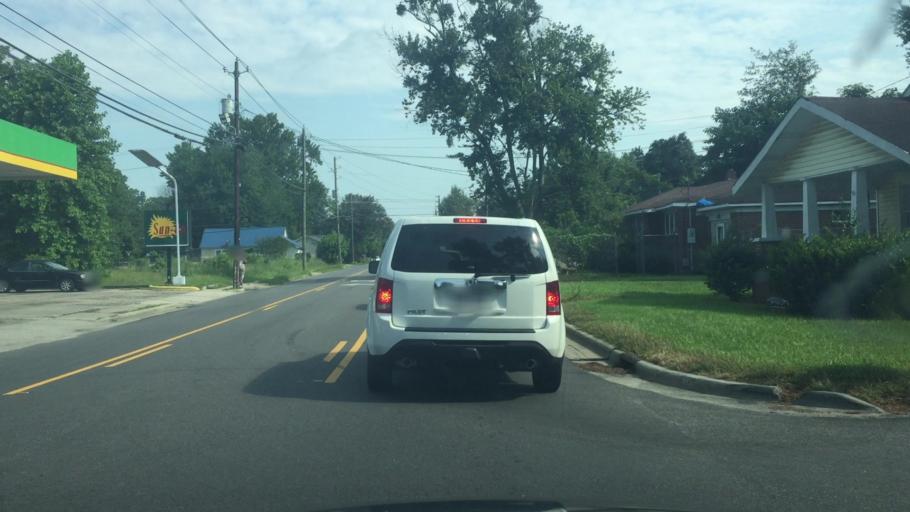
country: US
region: North Carolina
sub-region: Columbus County
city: Chadbourn
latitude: 34.3188
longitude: -78.8264
